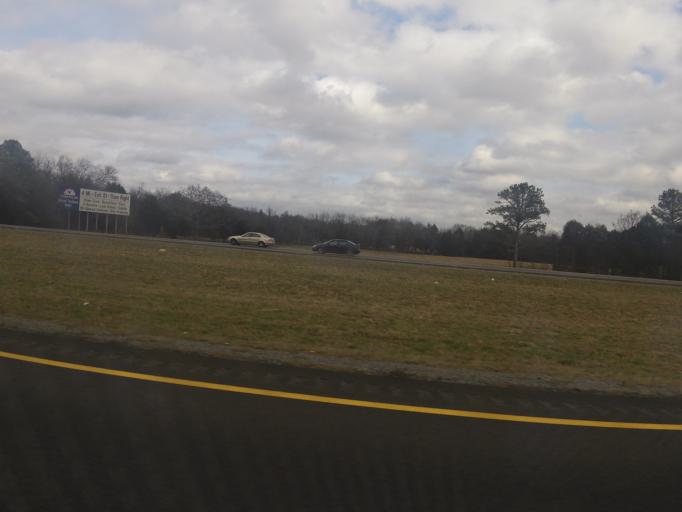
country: US
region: Tennessee
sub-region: Rutherford County
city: Plainview
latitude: 35.7507
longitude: -86.3435
